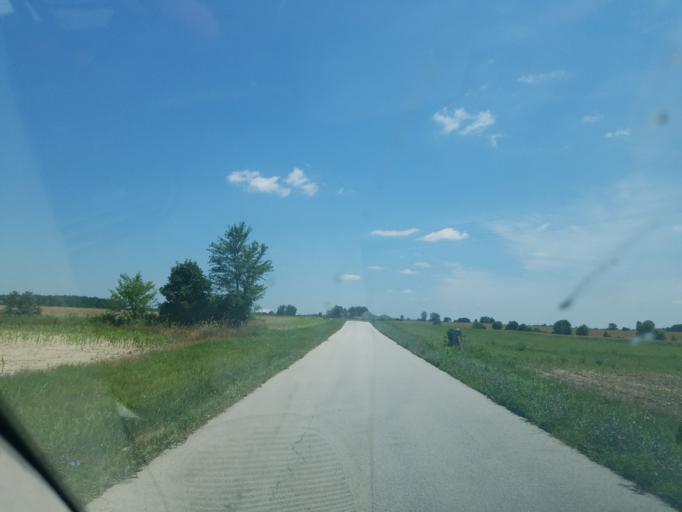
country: US
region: Ohio
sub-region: Hancock County
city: Arlington
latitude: 40.8483
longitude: -83.6098
